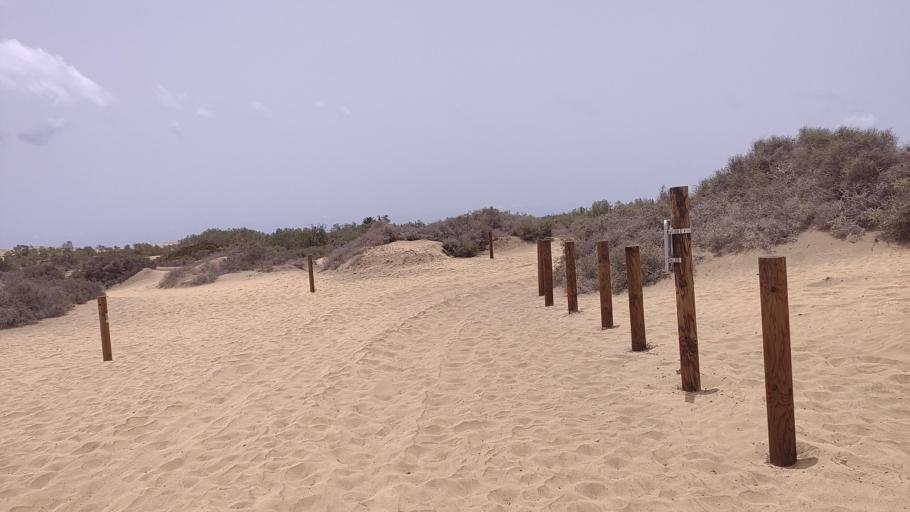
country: ES
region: Canary Islands
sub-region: Provincia de Las Palmas
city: Playa del Ingles
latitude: 27.7426
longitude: -15.5896
